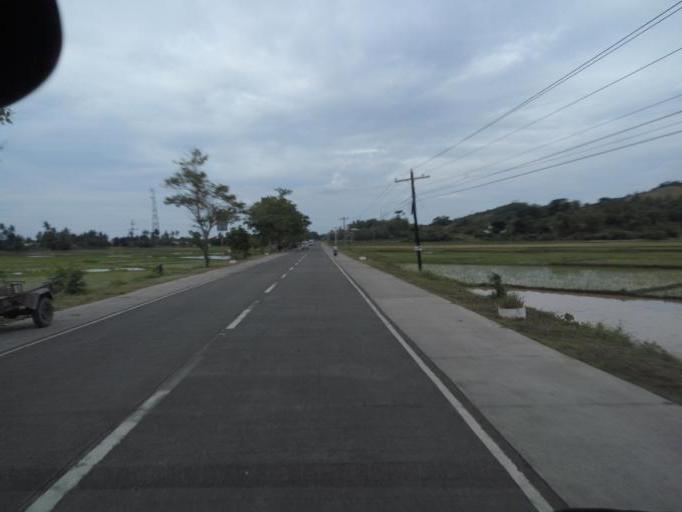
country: PH
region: Cagayan Valley
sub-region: Province of Cagayan
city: Gonzaga
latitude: 18.2748
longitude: 122.0064
